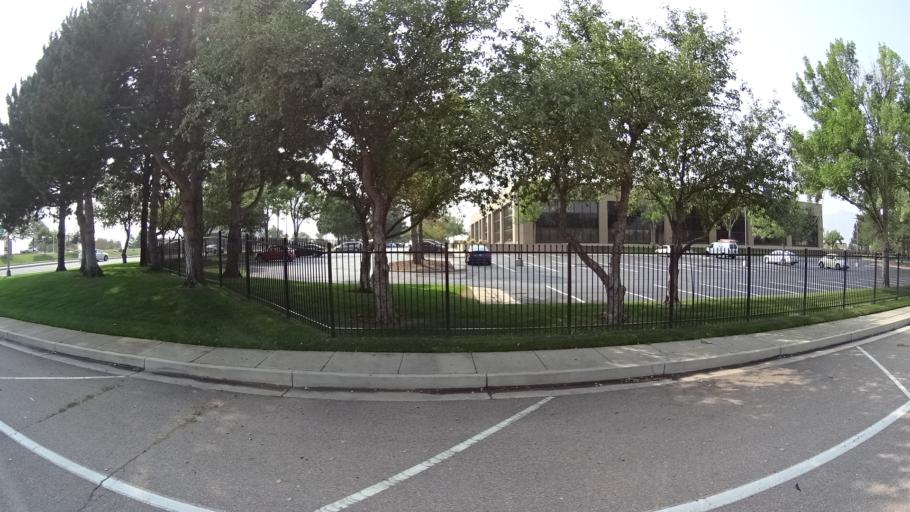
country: US
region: Colorado
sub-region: El Paso County
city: Stratmoor
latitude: 38.8169
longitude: -104.7581
